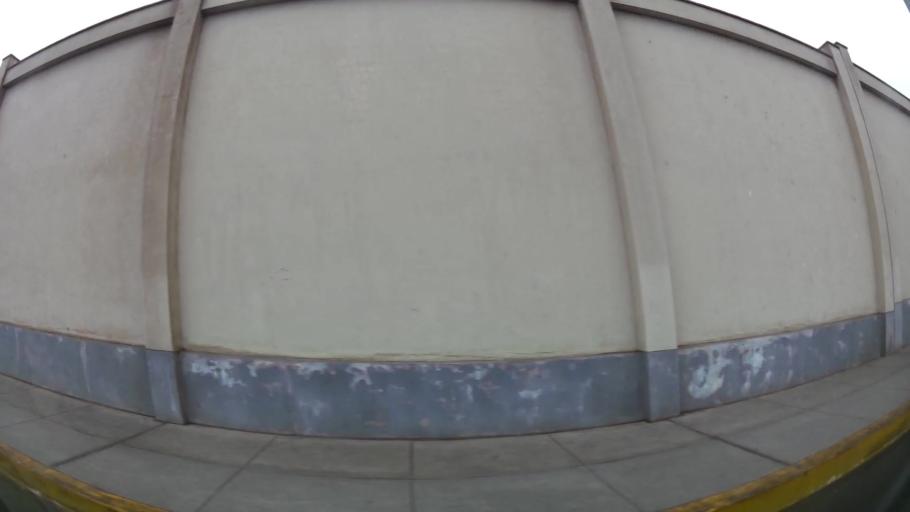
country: PE
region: Callao
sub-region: Callao
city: Callao
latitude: -12.0766
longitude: -77.1163
